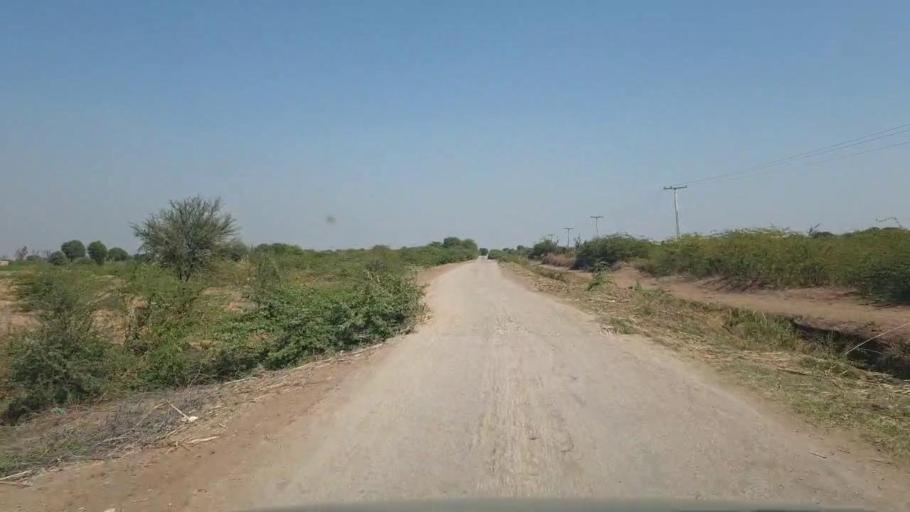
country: PK
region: Sindh
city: Digri
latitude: 25.0941
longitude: 69.2428
